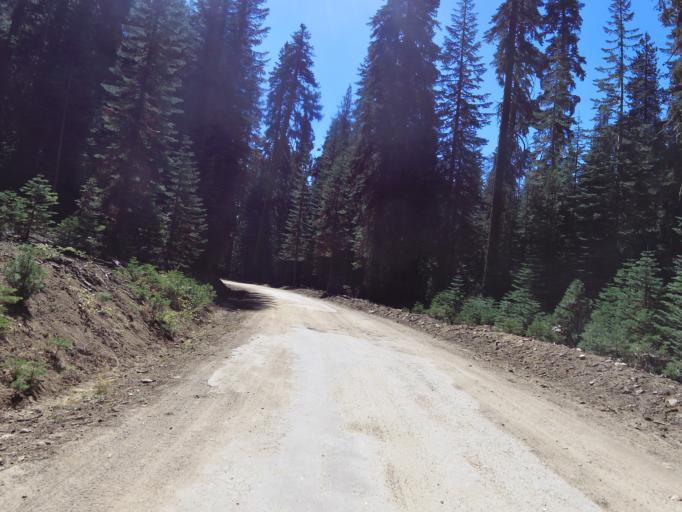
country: US
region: California
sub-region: Madera County
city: Oakhurst
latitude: 37.4169
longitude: -119.5002
